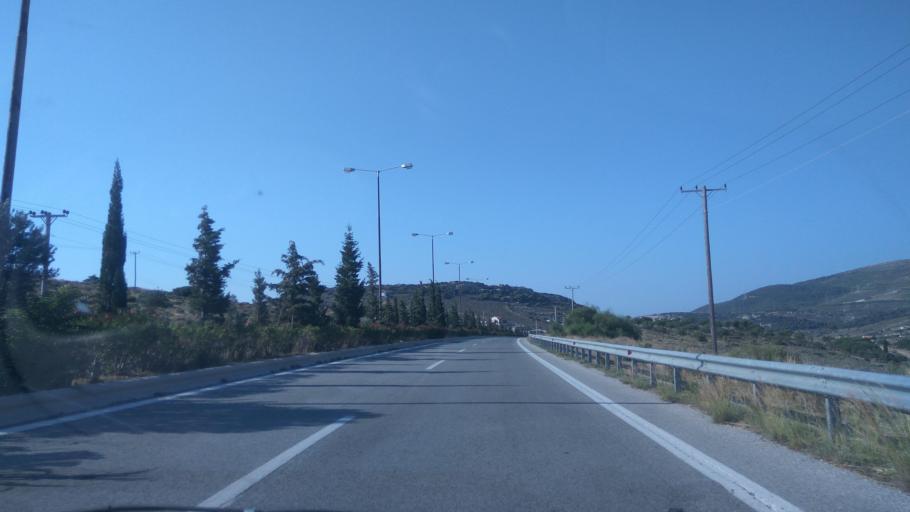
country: GR
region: Attica
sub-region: Nomarchia Anatolikis Attikis
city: Lavrio
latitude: 37.7851
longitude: 24.0576
